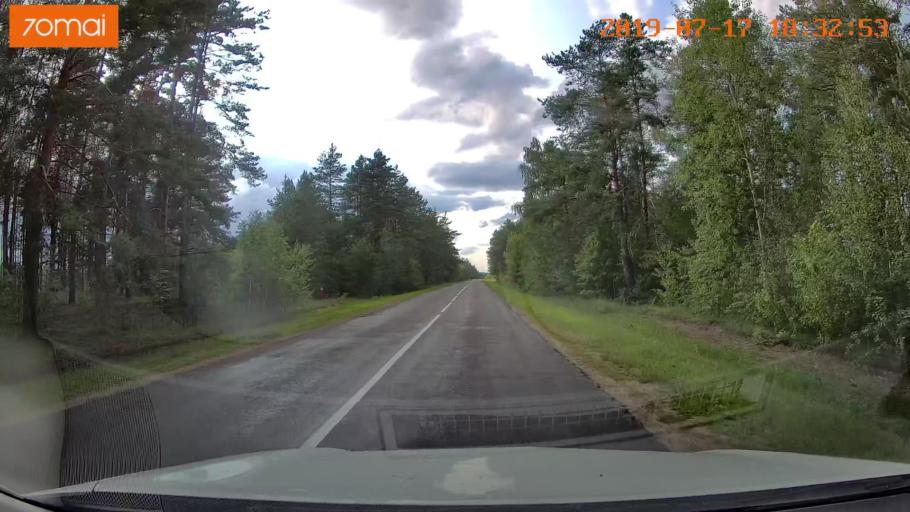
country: BY
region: Mogilev
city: Asipovichy
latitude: 53.2753
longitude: 28.6727
